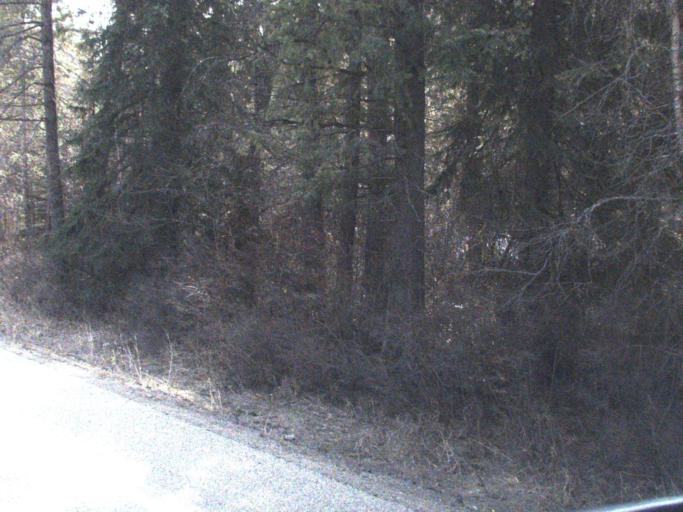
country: US
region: Washington
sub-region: Stevens County
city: Colville
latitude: 48.5153
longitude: -117.7498
